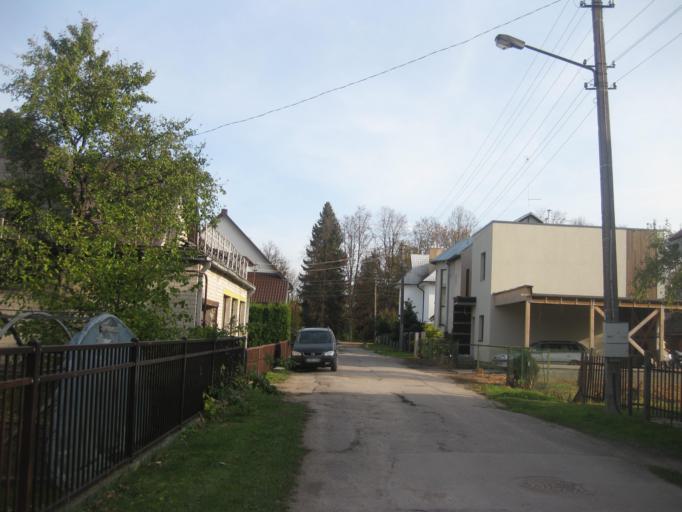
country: LT
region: Kauno apskritis
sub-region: Kaunas
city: Kaunas
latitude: 54.8926
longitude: 23.8781
